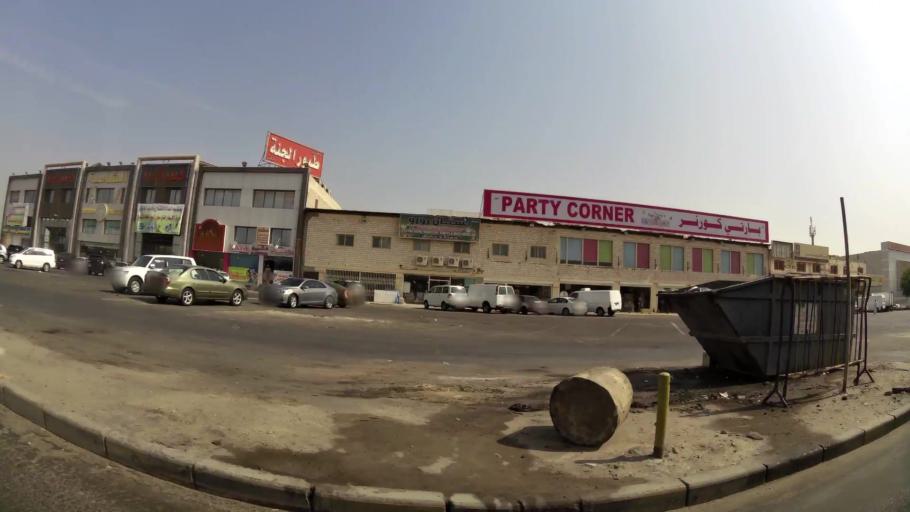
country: KW
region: Al Asimah
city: Ar Rabiyah
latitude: 29.3211
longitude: 47.9240
